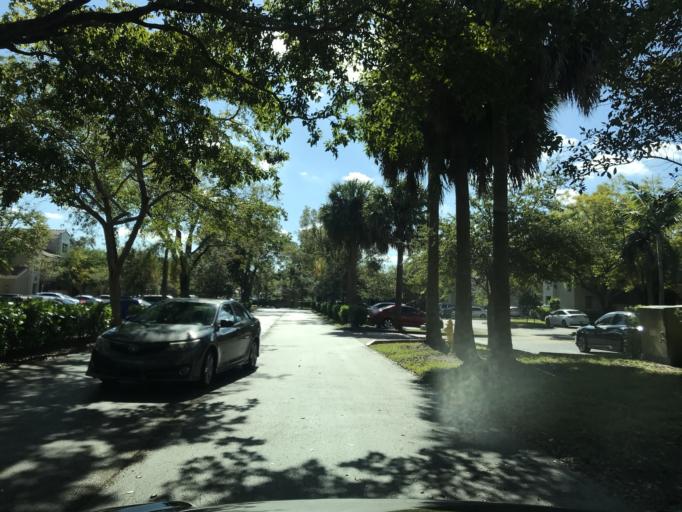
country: US
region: Florida
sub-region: Broward County
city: Pine Island Ridge
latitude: 26.1308
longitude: -80.2702
